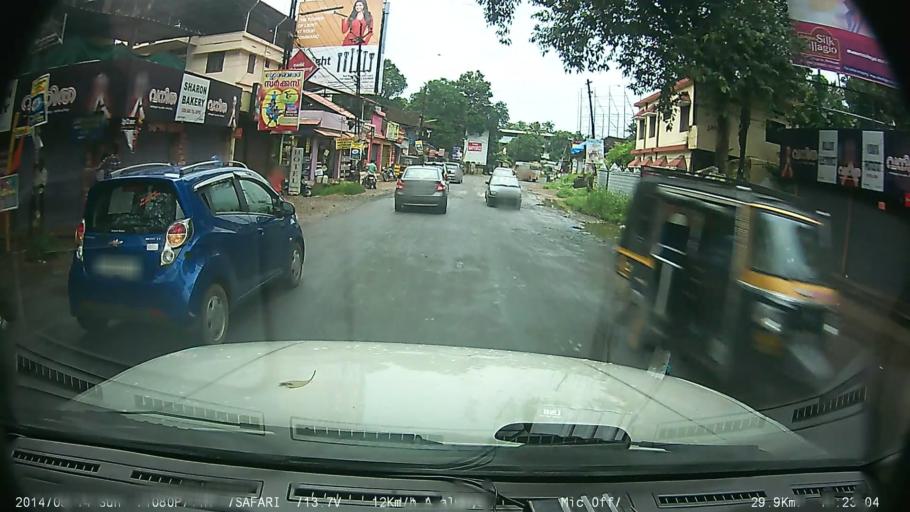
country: IN
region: Kerala
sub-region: Kottayam
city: Kottayam
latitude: 9.6115
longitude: 76.5334
